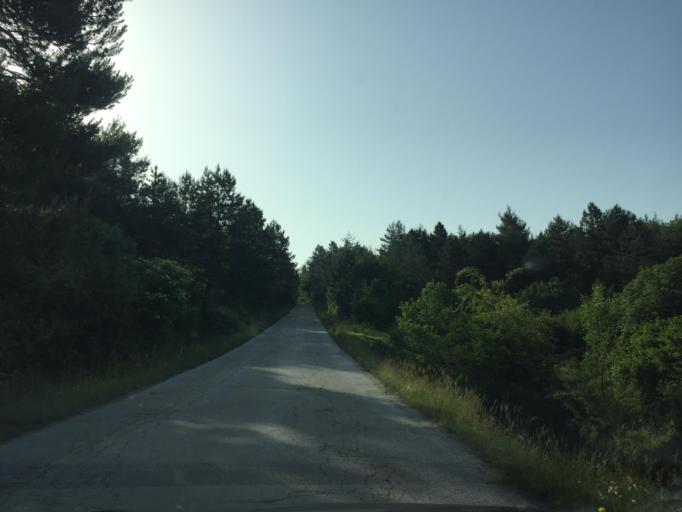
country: HR
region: Istarska
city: Buzet
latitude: 45.4787
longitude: 14.0649
